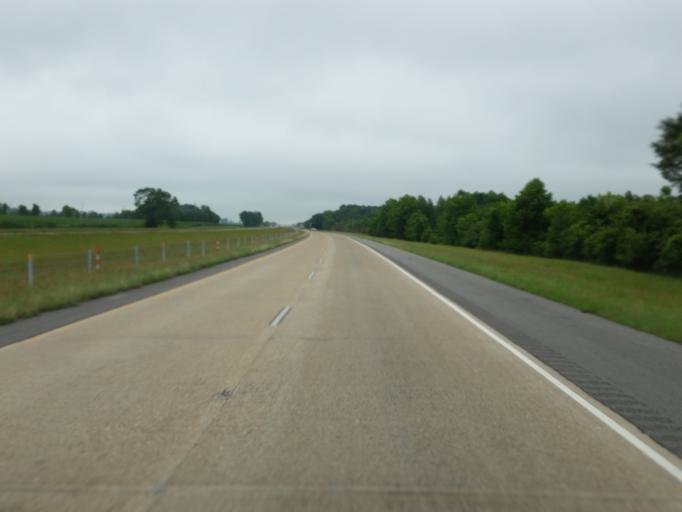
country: US
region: Louisiana
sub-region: Madison Parish
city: Tallulah
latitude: 32.3356
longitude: -91.0588
